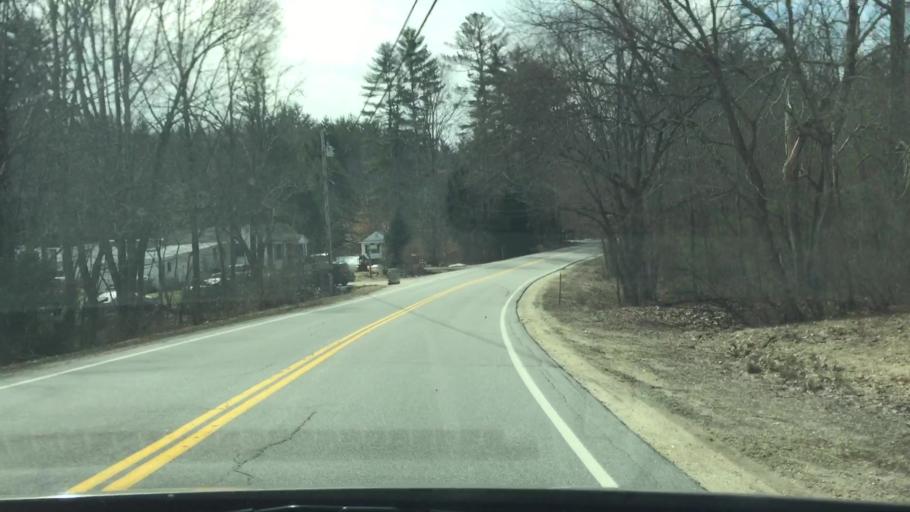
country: US
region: New Hampshire
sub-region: Strafford County
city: Barrington
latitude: 43.2364
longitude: -71.0564
